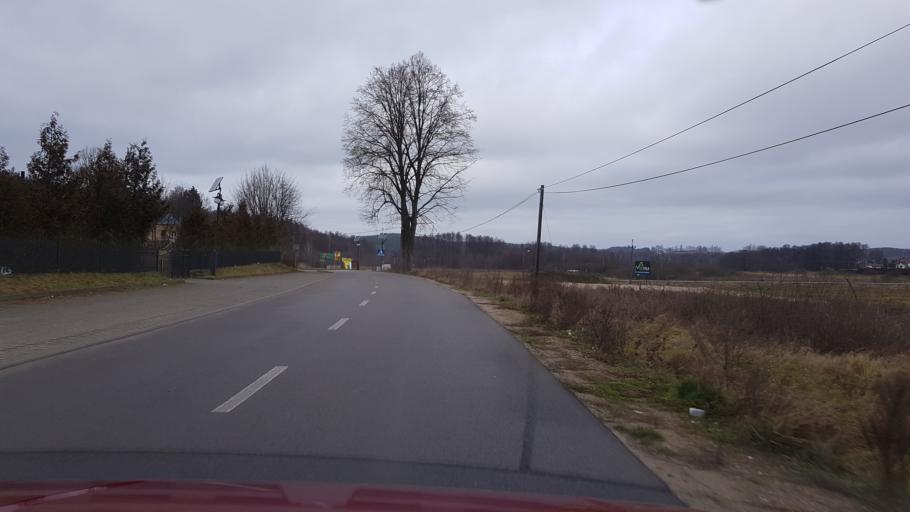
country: PL
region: Pomeranian Voivodeship
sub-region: Powiat bytowski
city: Borzytuchom
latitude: 54.1937
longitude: 17.3615
